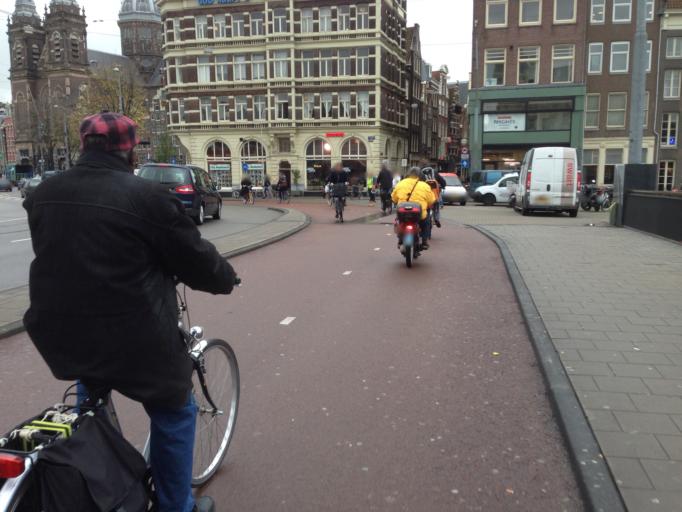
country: NL
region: North Holland
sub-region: Gemeente Amsterdam
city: Amsterdam
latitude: 52.3768
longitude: 4.8986
